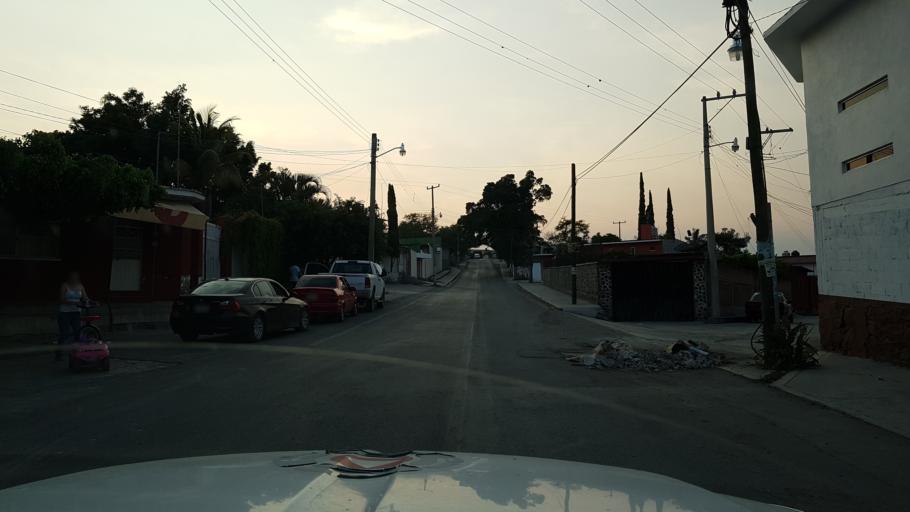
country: MX
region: Morelos
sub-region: Ayala
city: Abelardo L. Rodriguez
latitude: 18.7235
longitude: -98.9938
